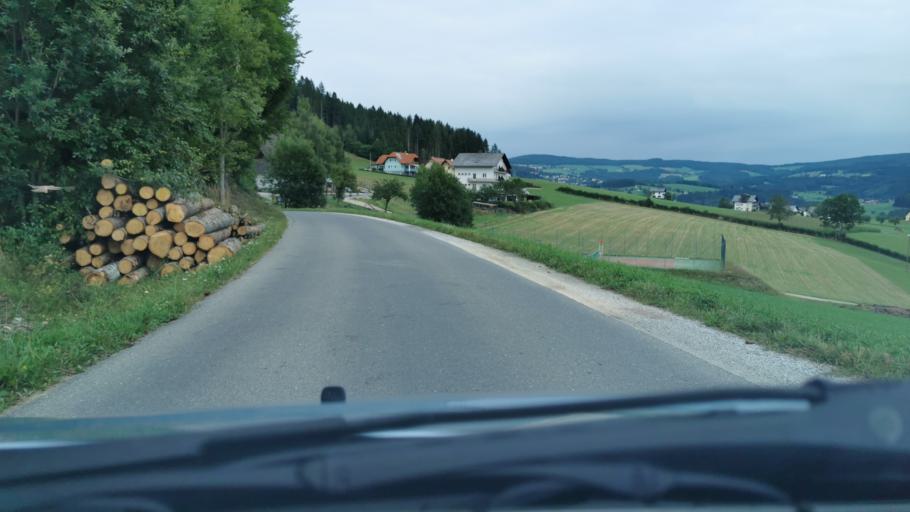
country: AT
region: Styria
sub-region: Politischer Bezirk Weiz
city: Strallegg
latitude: 47.3926
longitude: 15.6740
